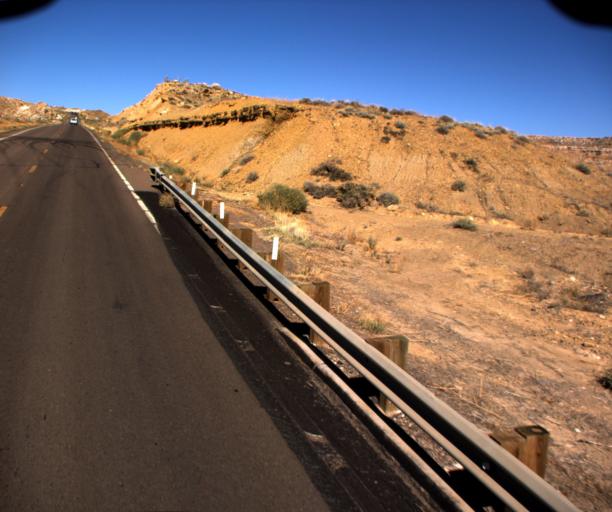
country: US
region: Arizona
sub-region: Navajo County
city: First Mesa
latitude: 35.7986
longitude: -110.5135
